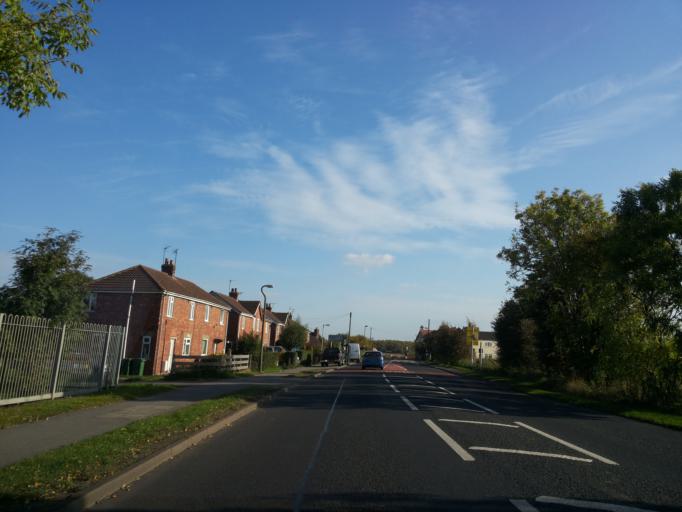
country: GB
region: England
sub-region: East Riding of Yorkshire
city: Snaith
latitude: 53.6858
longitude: -0.9981
